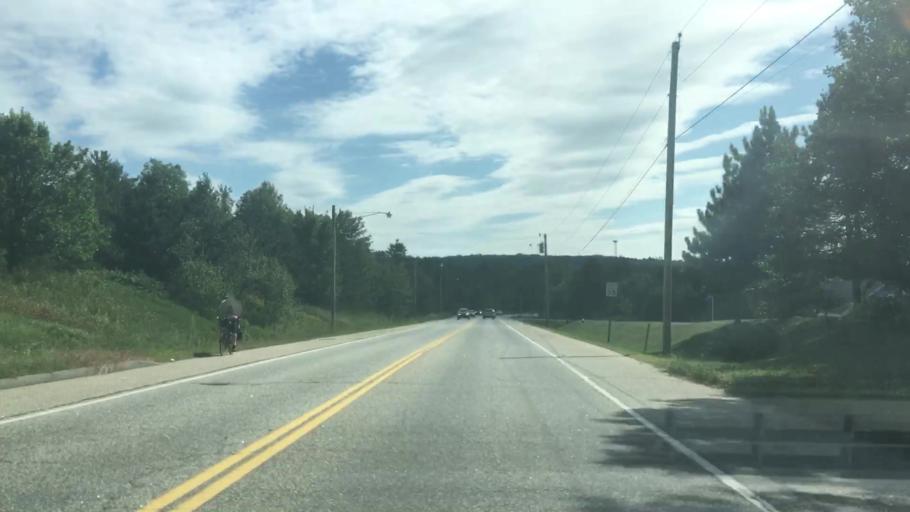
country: US
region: Maine
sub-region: Androscoggin County
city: Lewiston
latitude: 44.0819
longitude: -70.1782
